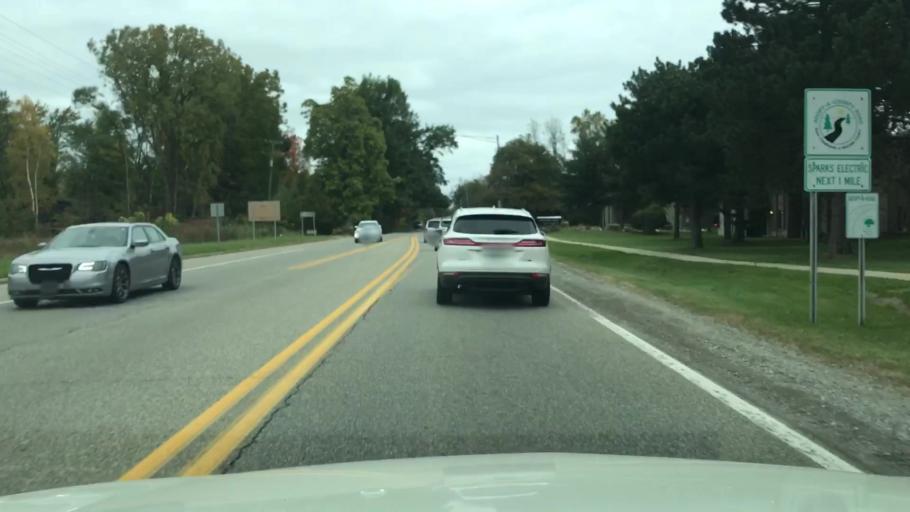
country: US
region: Michigan
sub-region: Macomb County
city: Utica
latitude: 42.6284
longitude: -83.0720
